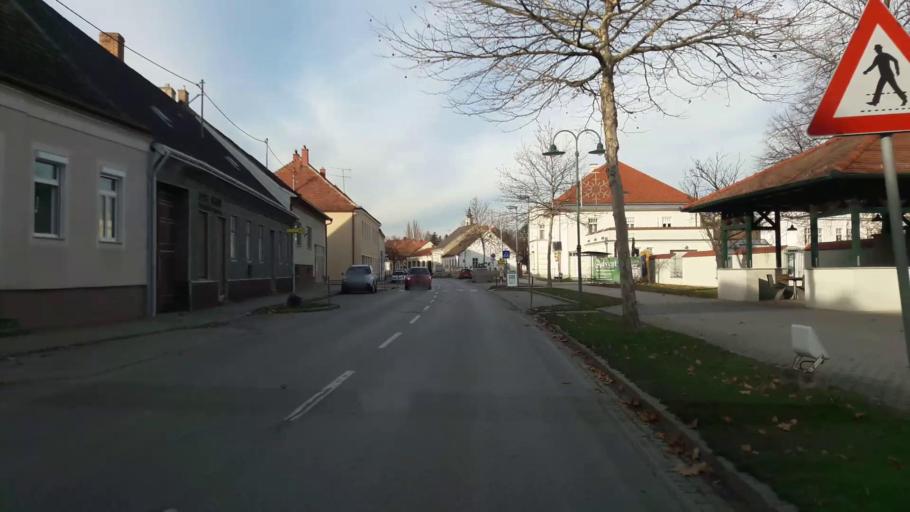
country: AT
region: Lower Austria
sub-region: Politischer Bezirk Ganserndorf
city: Bad Pirawarth
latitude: 48.4519
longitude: 16.6002
